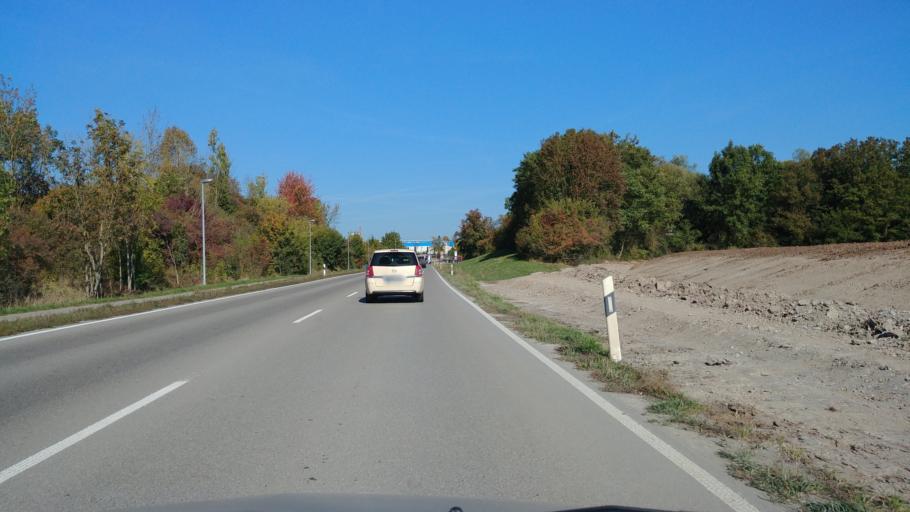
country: DE
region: Baden-Wuerttemberg
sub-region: Regierungsbezirk Stuttgart
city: Gaildorf
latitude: 48.9915
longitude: 9.7742
